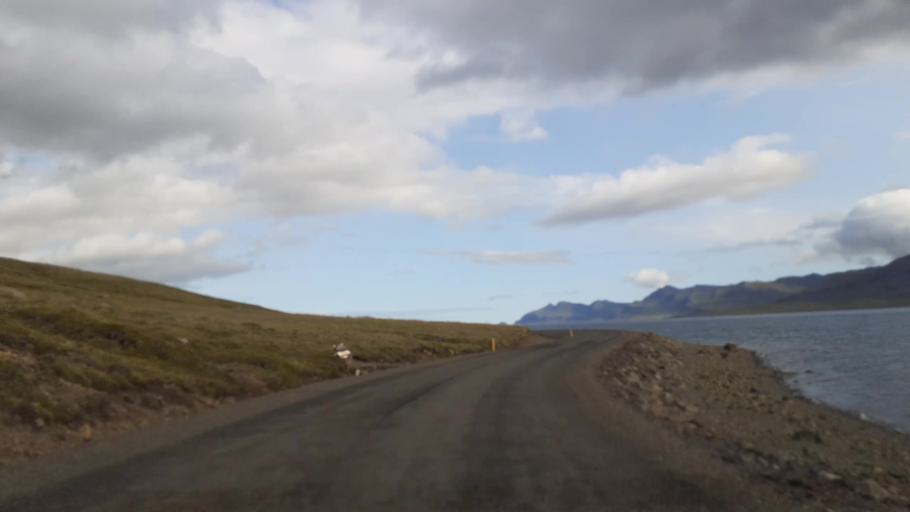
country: IS
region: East
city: Eskifjoerdur
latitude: 65.0577
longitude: -13.9839
